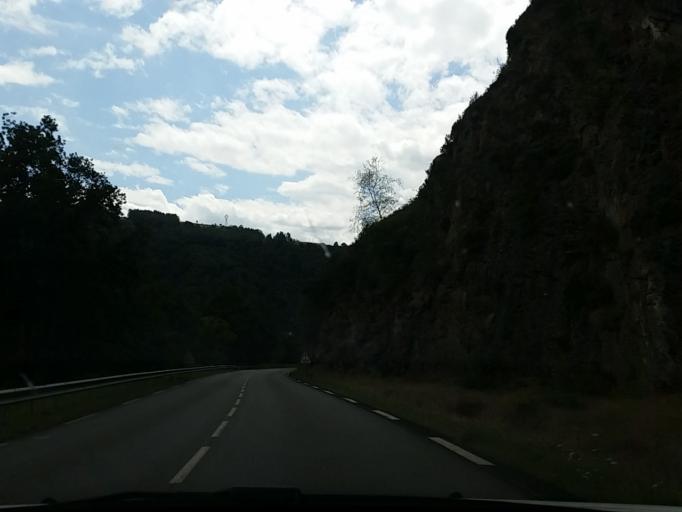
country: FR
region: Auvergne
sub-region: Departement du Cantal
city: Neuveglise
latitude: 44.8976
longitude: 3.0049
